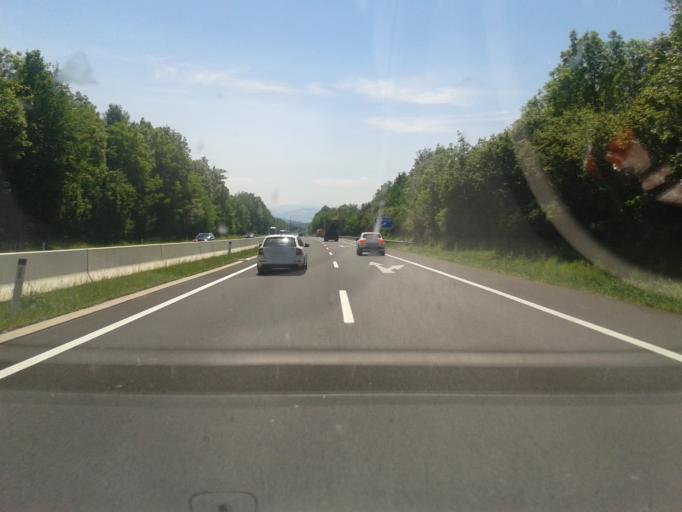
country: AT
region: Carinthia
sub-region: Politischer Bezirk Wolfsberg
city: Wolfsberg
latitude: 46.8260
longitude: 14.8187
